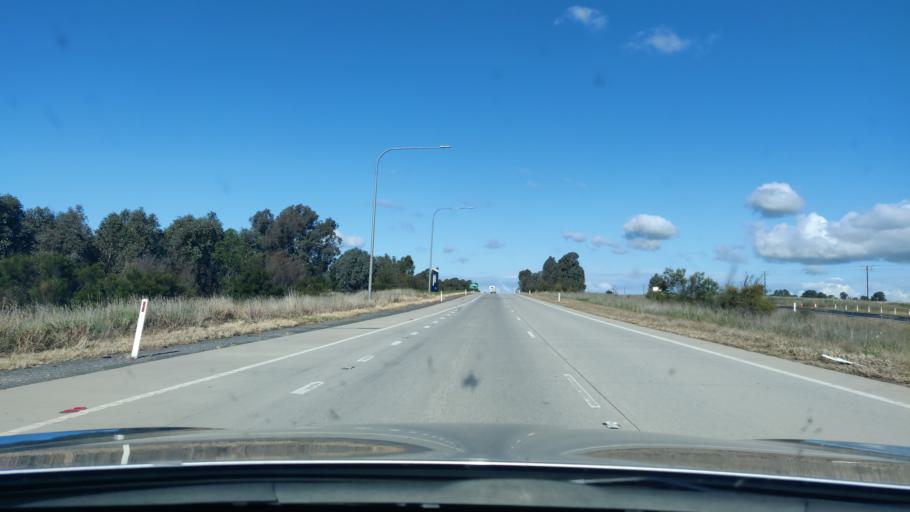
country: AU
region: New South Wales
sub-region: Greater Hume Shire
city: Jindera
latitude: -35.9388
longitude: 147.0033
